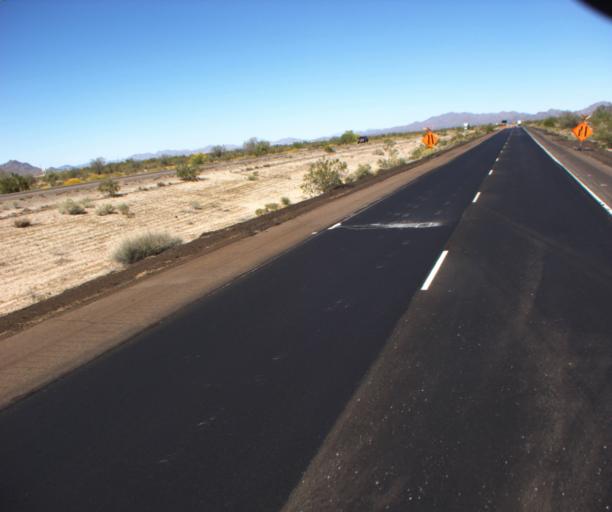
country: US
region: Arizona
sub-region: Maricopa County
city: Gila Bend
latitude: 32.9922
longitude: -112.6628
